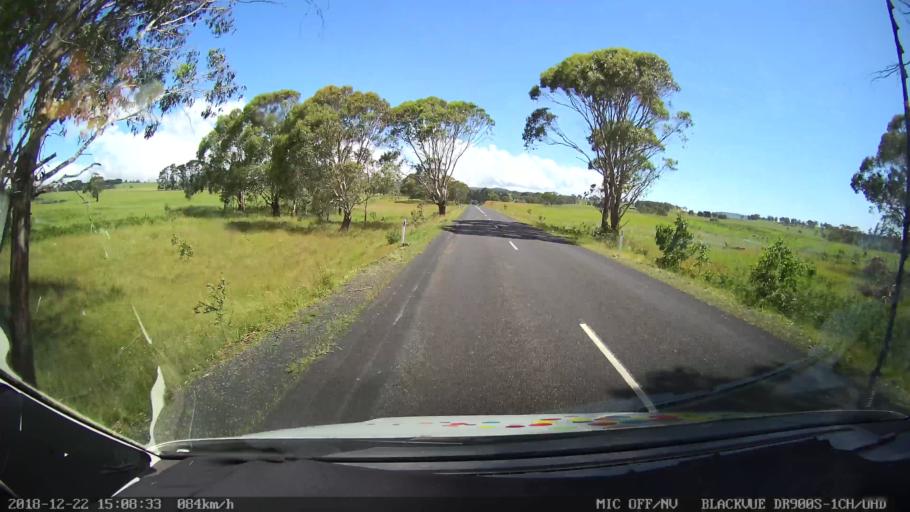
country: AU
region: New South Wales
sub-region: Bellingen
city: Dorrigo
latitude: -30.3138
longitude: 152.4134
